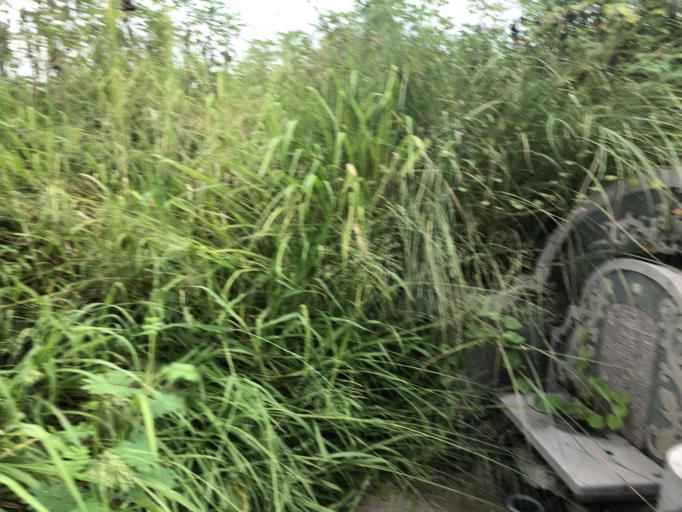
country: TW
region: Taiwan
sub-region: Tainan
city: Tainan
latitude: 22.9655
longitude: 120.1992
